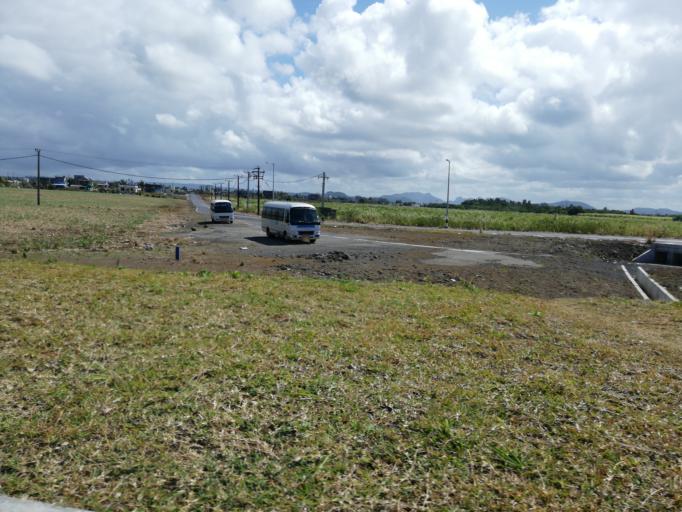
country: MU
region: Grand Port
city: Plaine Magnien
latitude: -20.4393
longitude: 57.6708
